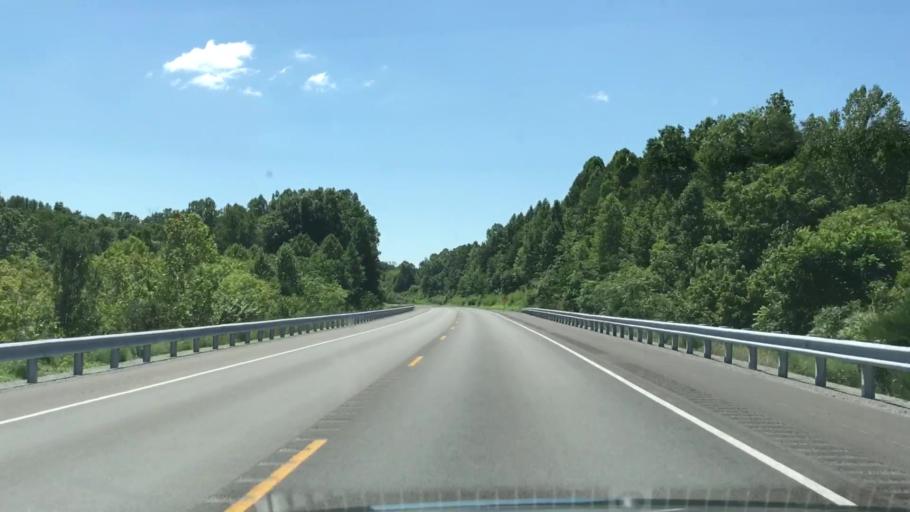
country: US
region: Kentucky
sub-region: Cumberland County
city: Burkesville
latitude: 36.6877
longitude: -85.3744
